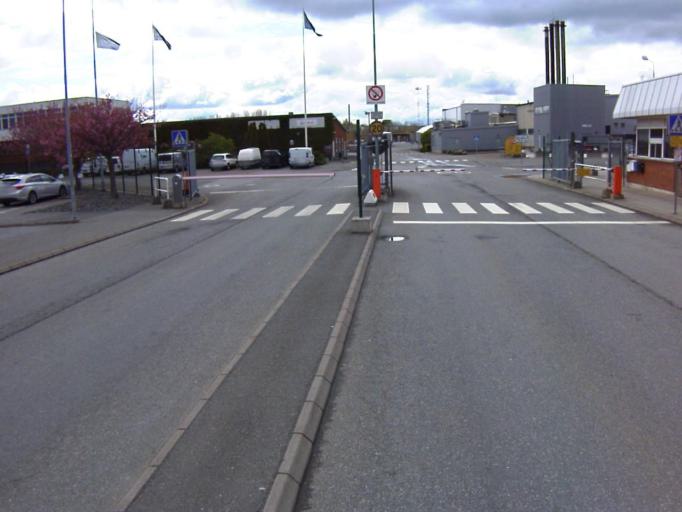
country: SE
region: Skane
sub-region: Kristianstads Kommun
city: Kristianstad
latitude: 56.0211
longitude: 14.1478
